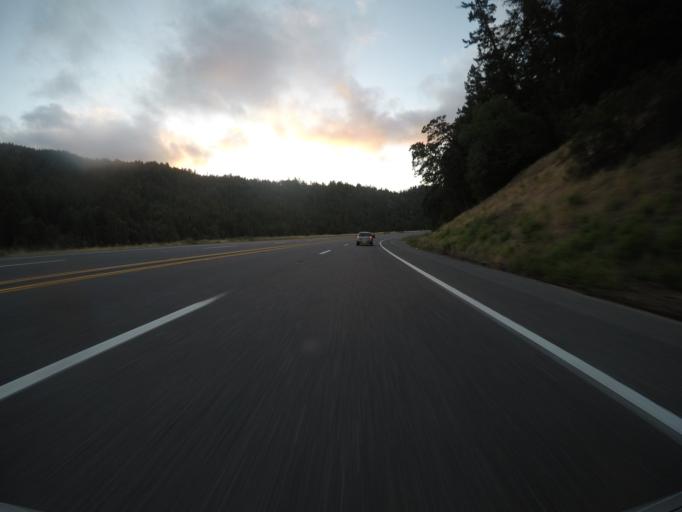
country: US
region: California
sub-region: Humboldt County
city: Redway
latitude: 40.0500
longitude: -123.7916
